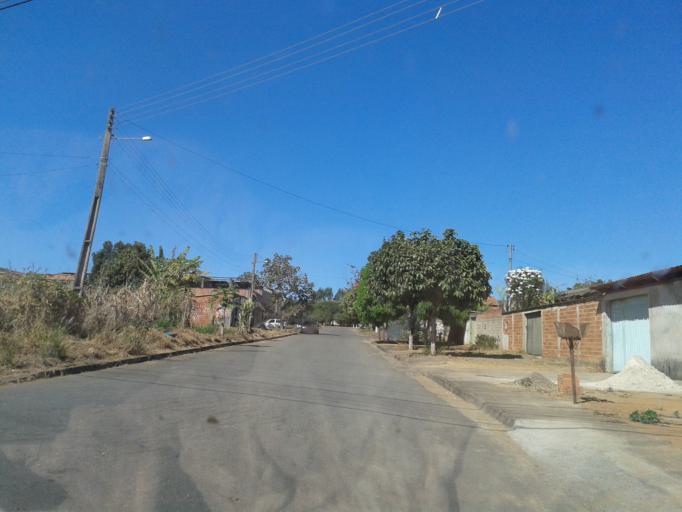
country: BR
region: Goias
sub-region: Aparecida De Goiania
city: Aparecida de Goiania
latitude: -16.7900
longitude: -49.2396
